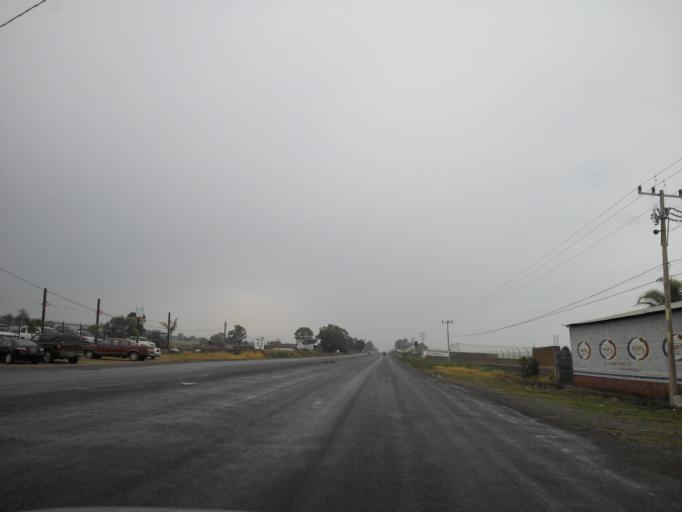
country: MX
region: Jalisco
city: Capilla de Guadalupe
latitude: 20.8350
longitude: -102.6045
